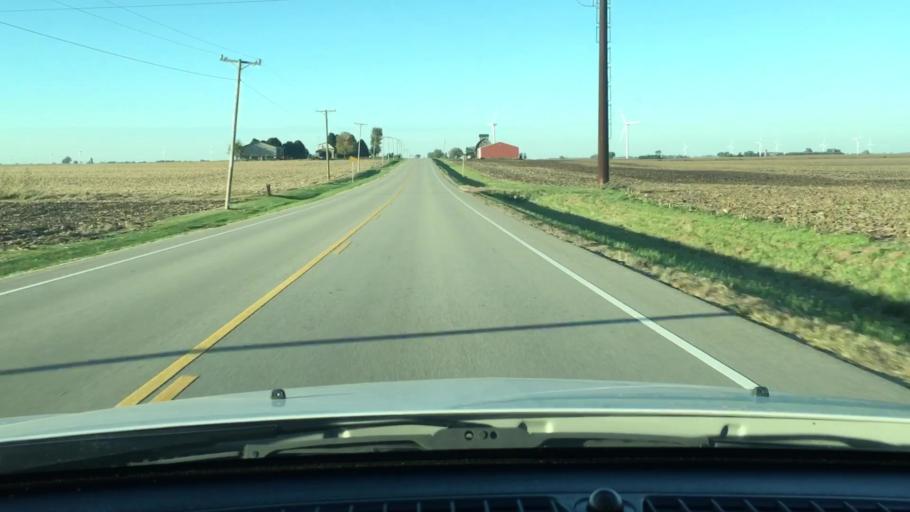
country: US
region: Illinois
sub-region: DeKalb County
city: Malta
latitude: 41.8261
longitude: -88.8864
